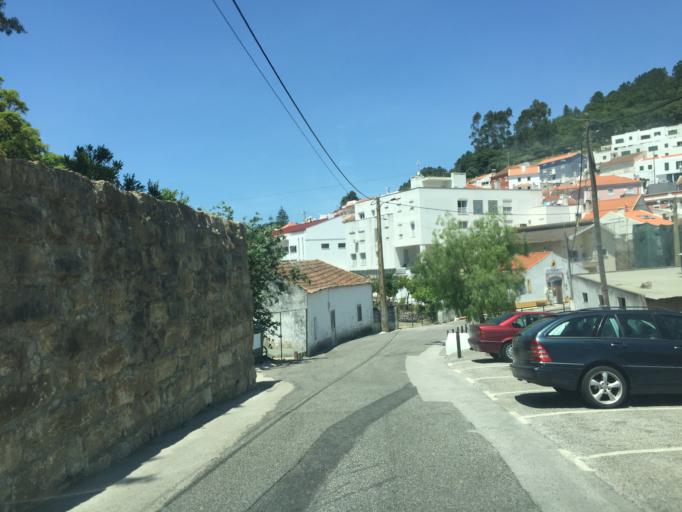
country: PT
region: Lisbon
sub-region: Mafra
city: Venda do Pinheiro
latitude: 38.8887
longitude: -9.2073
